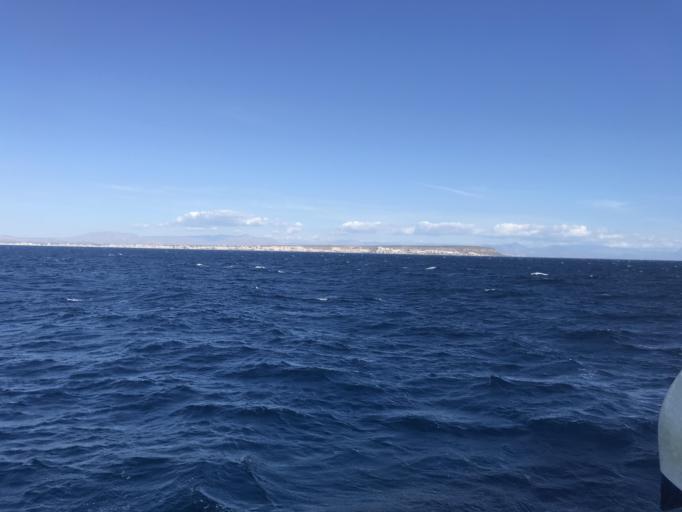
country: ES
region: Valencia
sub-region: Provincia de Alicante
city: Santa Pola
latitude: 38.1317
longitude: -0.5350
